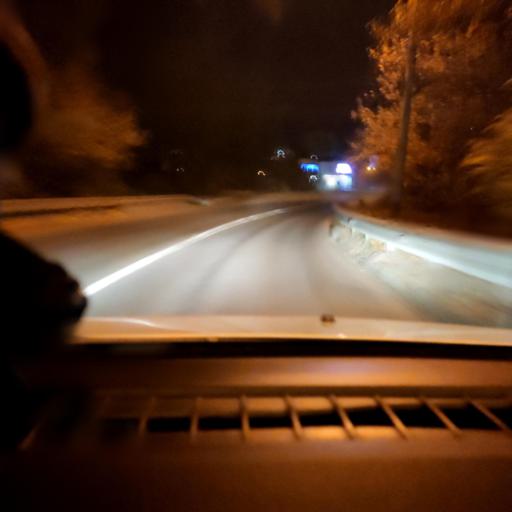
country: RU
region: Samara
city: Rozhdestveno
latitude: 53.1502
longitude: 50.0664
